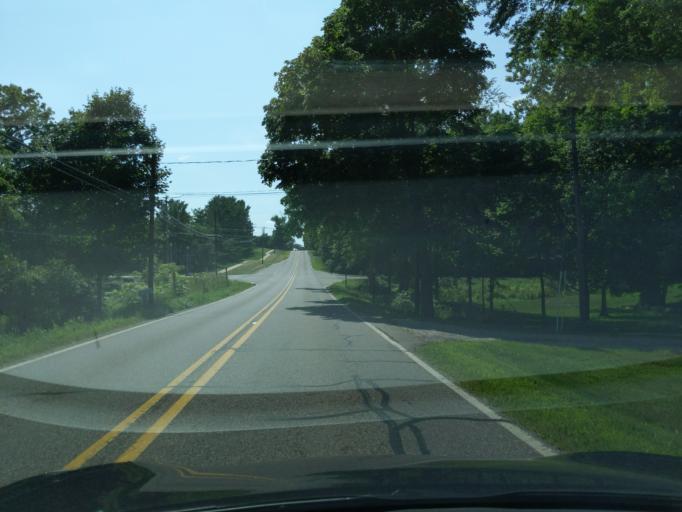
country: US
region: Michigan
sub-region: Eaton County
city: Grand Ledge
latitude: 42.7485
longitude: -84.7289
